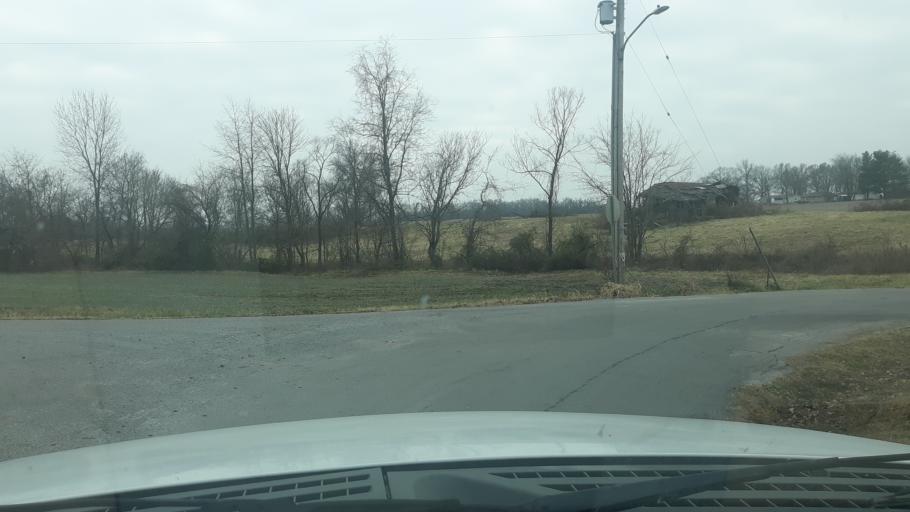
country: US
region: Illinois
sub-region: Saline County
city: Harrisburg
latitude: 37.8379
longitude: -88.6055
